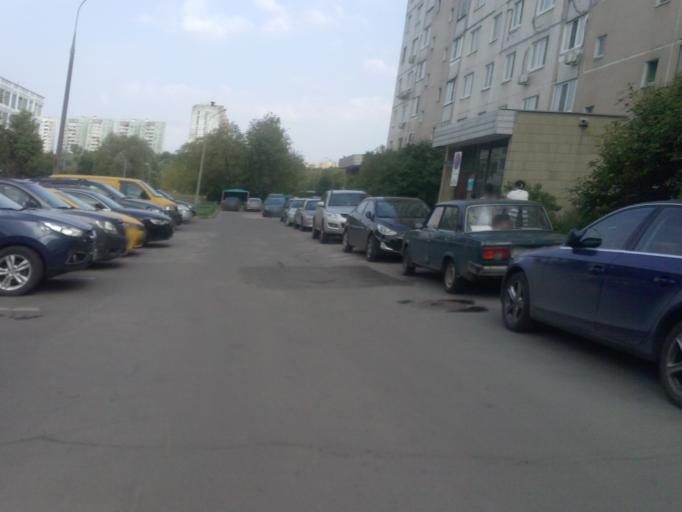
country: RU
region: Moskovskaya
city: Bol'shaya Setun'
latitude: 55.7154
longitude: 37.4147
